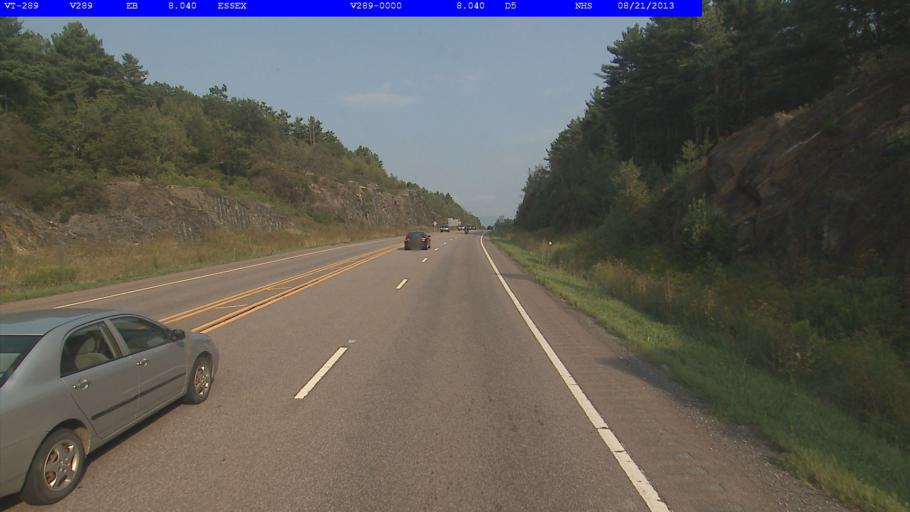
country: US
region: Vermont
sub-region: Chittenden County
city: Essex Junction
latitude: 44.5170
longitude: -73.1127
